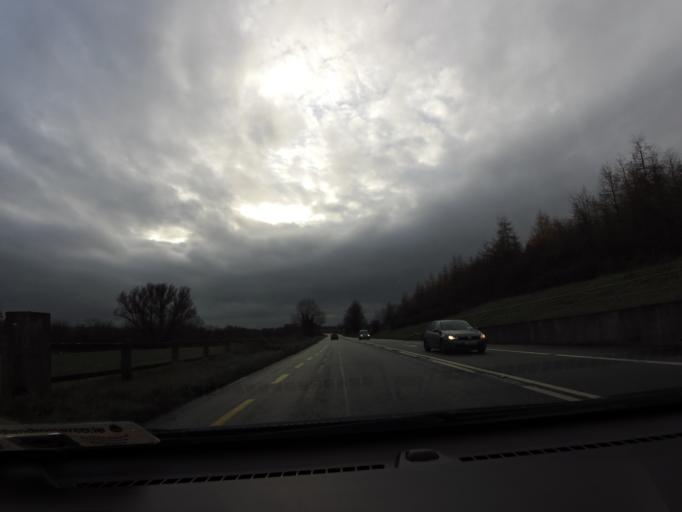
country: IE
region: Leinster
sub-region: Kilkenny
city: Ballyragget
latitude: 52.7978
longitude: -7.3496
